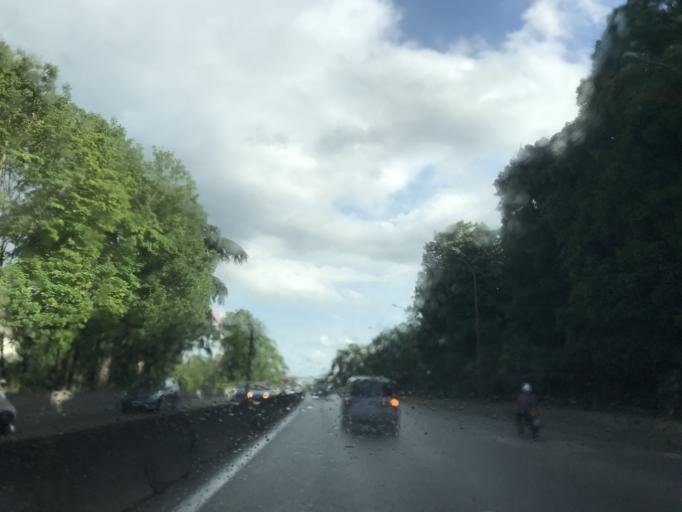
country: FR
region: Ile-de-France
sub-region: Departement des Hauts-de-Seine
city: Meudon
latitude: 48.7962
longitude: 2.2174
